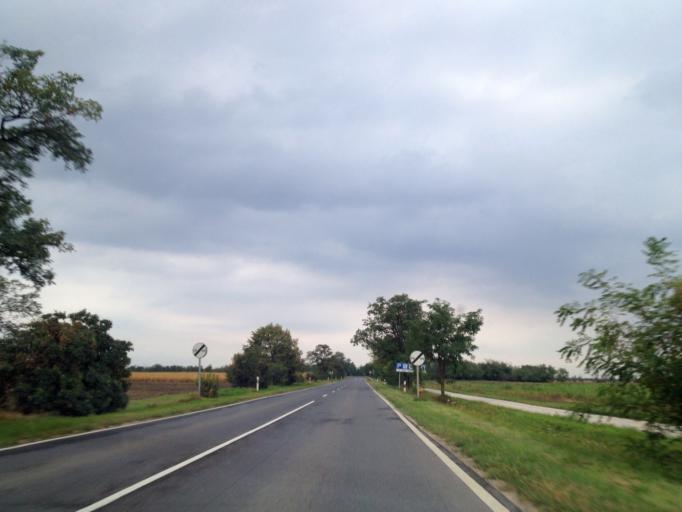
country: HU
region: Gyor-Moson-Sopron
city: Mosonmagyarovar
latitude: 47.9036
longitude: 17.1944
